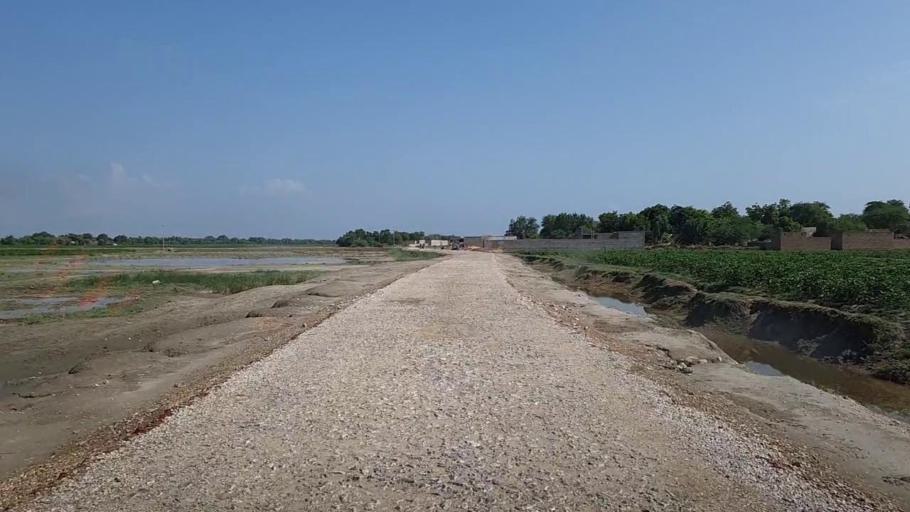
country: PK
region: Sindh
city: Bhiria
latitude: 26.8713
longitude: 68.2333
